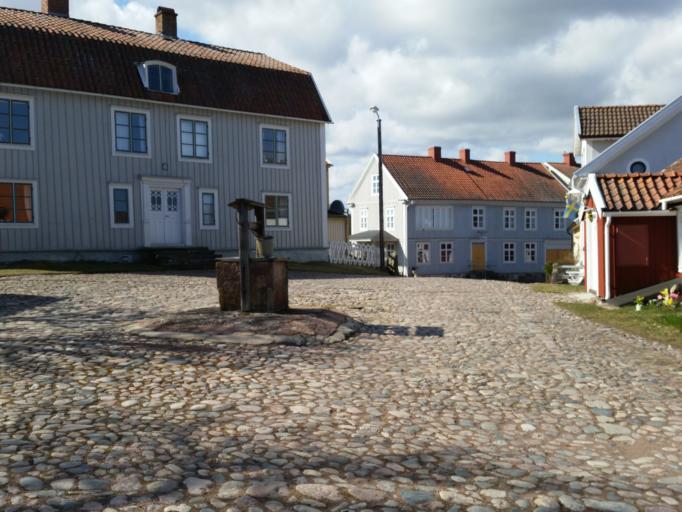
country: SE
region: Kalmar
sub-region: Monsteras Kommun
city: Timmernabben
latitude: 56.9165
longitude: 16.4307
